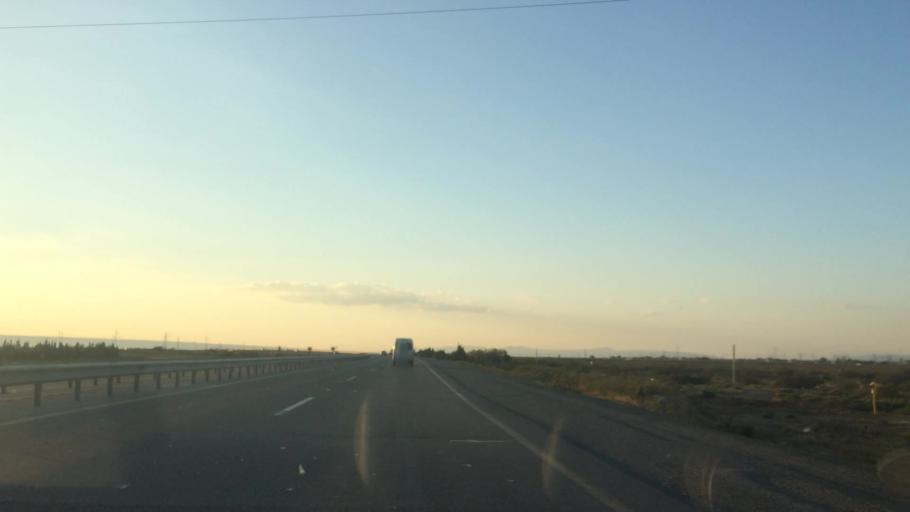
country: AZ
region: Baki
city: Qobustan
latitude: 39.9809
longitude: 49.2365
